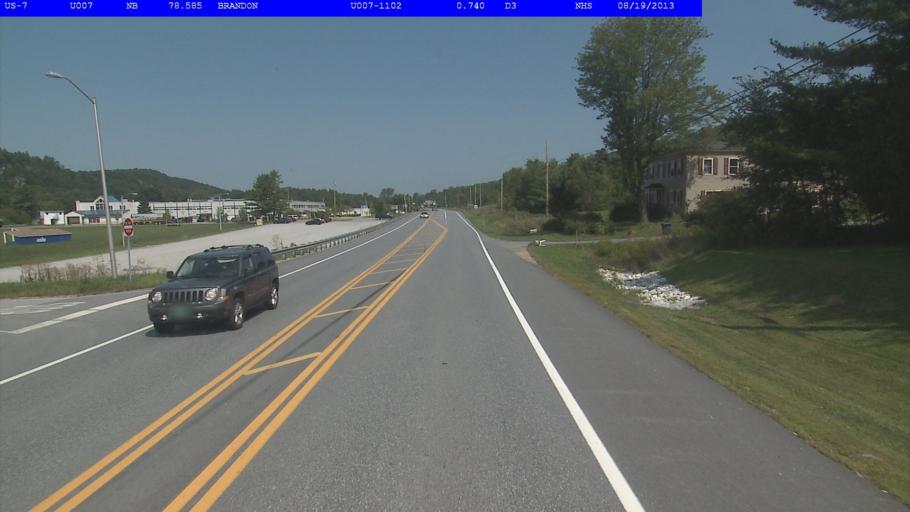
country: US
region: Vermont
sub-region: Rutland County
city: Brandon
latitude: 43.7650
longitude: -73.0502
